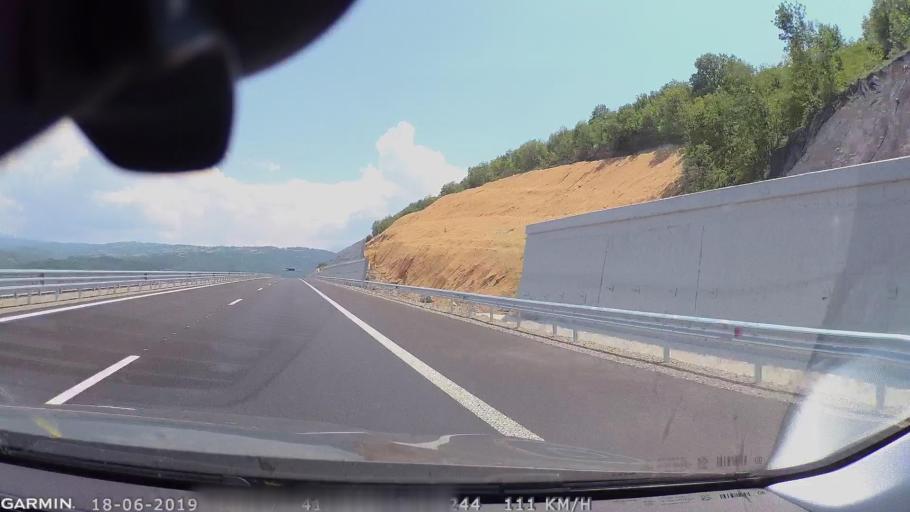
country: BG
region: Blagoevgrad
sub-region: Obshtina Blagoevgrad
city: Blagoevgrad
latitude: 41.9755
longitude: 23.0732
